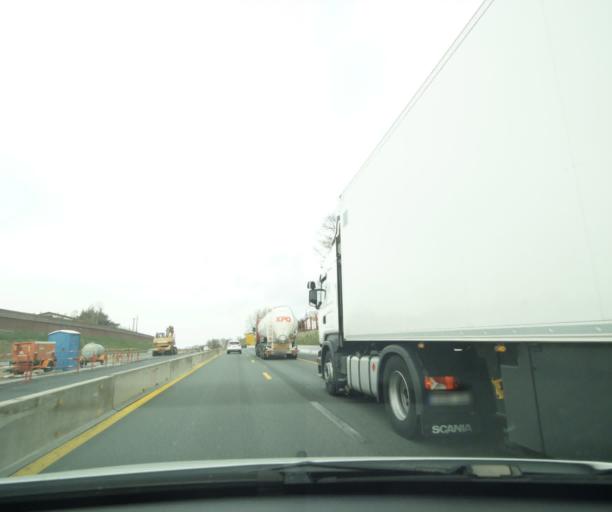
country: FR
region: Aquitaine
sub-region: Departement des Pyrenees-Atlantiques
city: Saint-Jean-de-Luz
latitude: 43.3904
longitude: -1.6396
